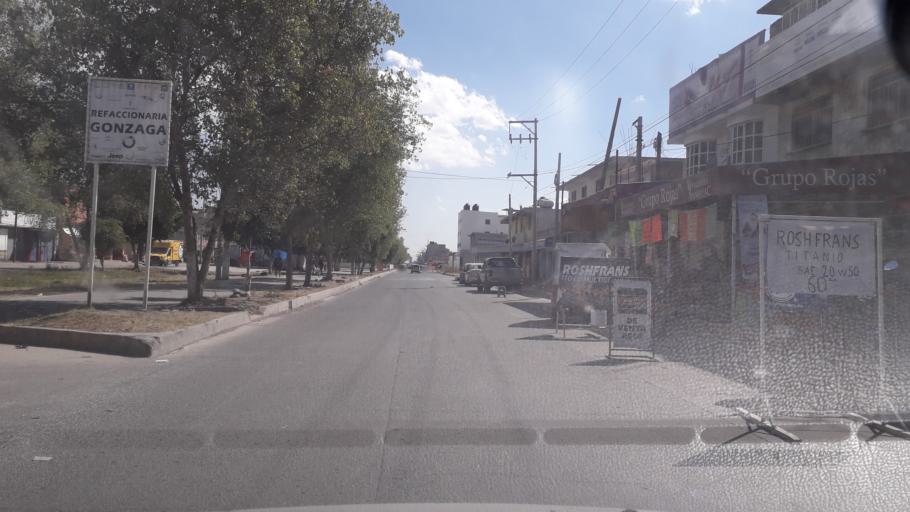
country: MX
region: Mexico
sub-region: Jaltenco
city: Alborada Jaltenco
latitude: 19.6543
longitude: -99.0669
